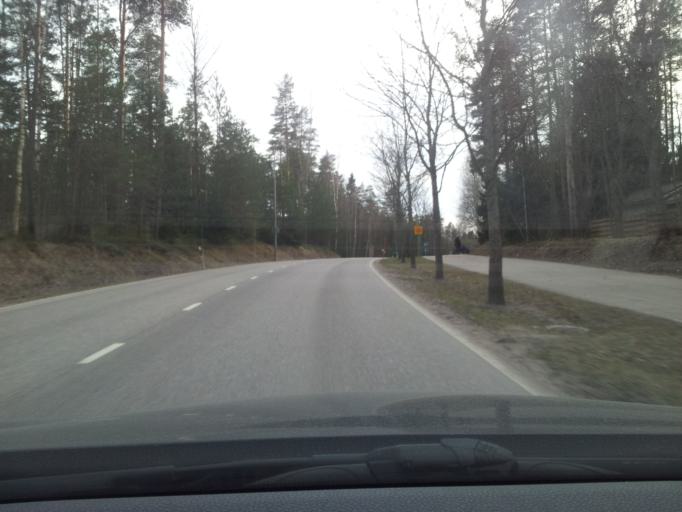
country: FI
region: Uusimaa
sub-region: Helsinki
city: Espoo
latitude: 60.1675
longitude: 24.6912
